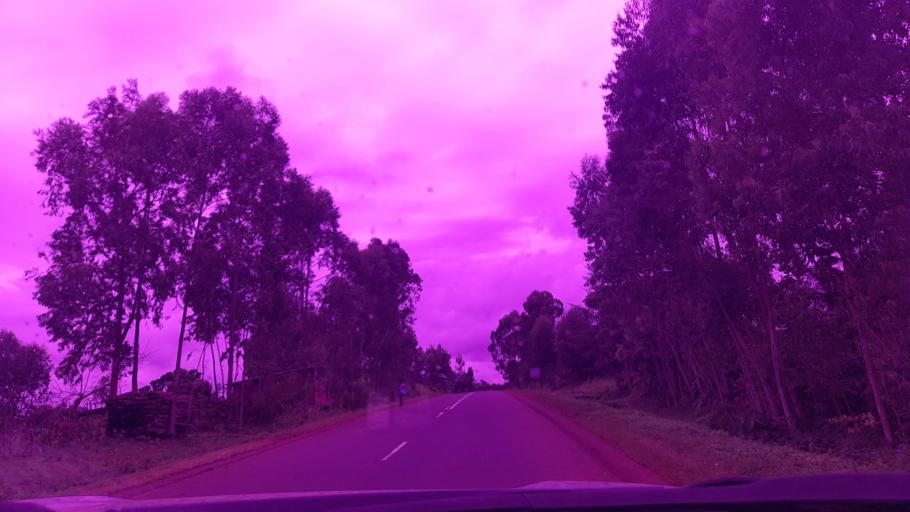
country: ET
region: Southern Nations, Nationalities, and People's Region
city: Bonga
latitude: 7.3019
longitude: 35.9929
